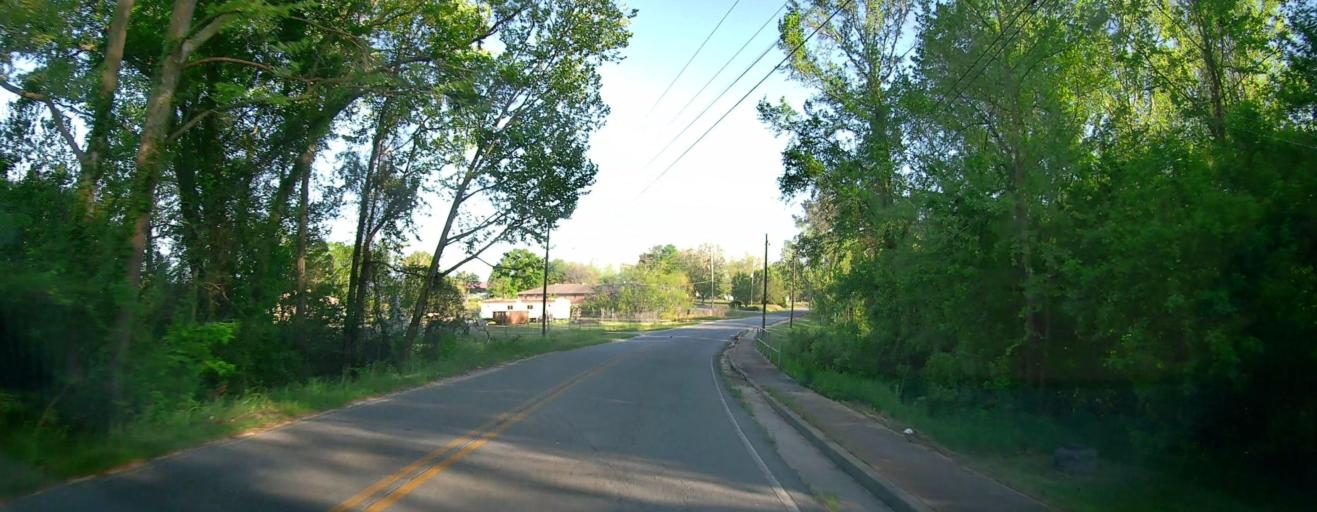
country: US
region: Georgia
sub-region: Macon County
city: Oglethorpe
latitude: 32.2924
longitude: -84.0592
